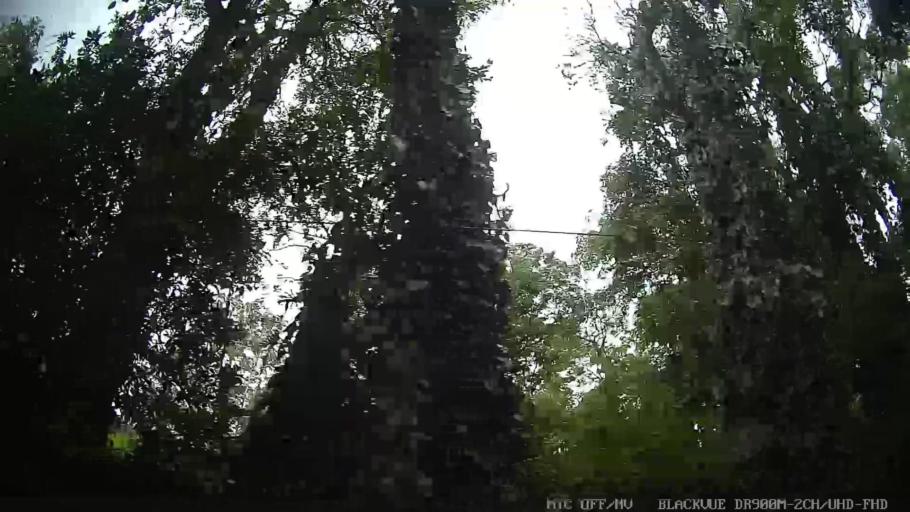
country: BR
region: Sao Paulo
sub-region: Itatiba
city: Itatiba
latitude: -23.0398
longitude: -46.8936
